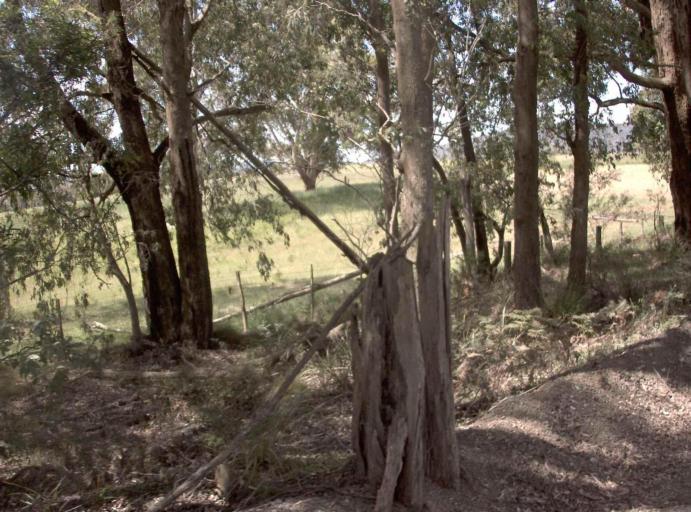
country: AU
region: New South Wales
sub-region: Bombala
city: Bombala
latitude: -37.1838
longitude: 148.7178
